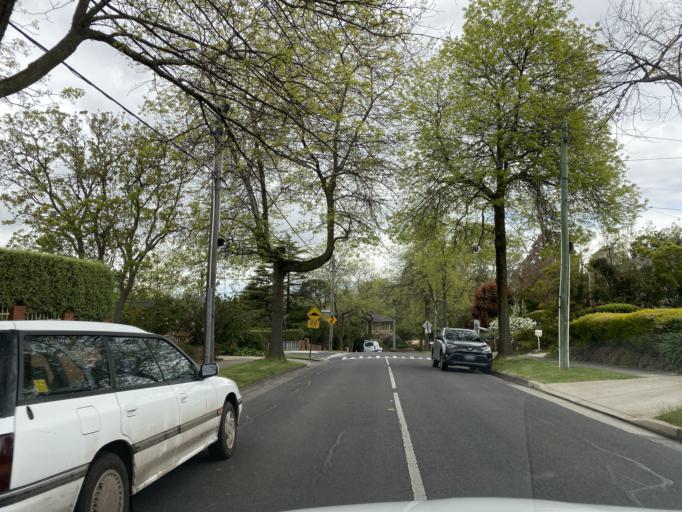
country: AU
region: Victoria
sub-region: Whitehorse
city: Box Hill South
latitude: -37.8345
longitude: 145.1163
